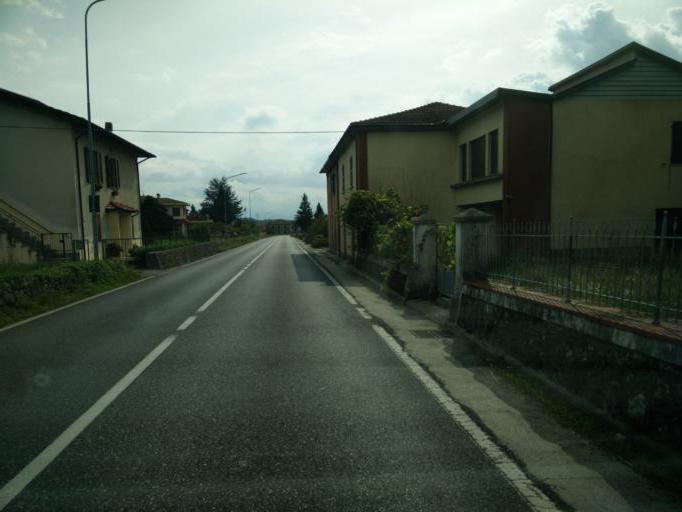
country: IT
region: Tuscany
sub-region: Provincia di Massa-Carrara
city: Pontremoli
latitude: 44.3547
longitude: 9.9043
